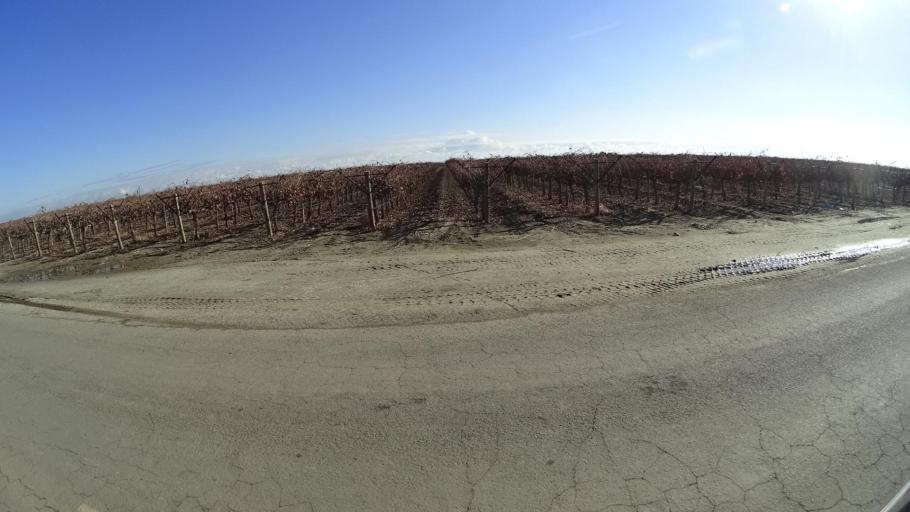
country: US
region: California
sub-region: Kern County
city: Delano
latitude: 35.7201
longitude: -119.2764
